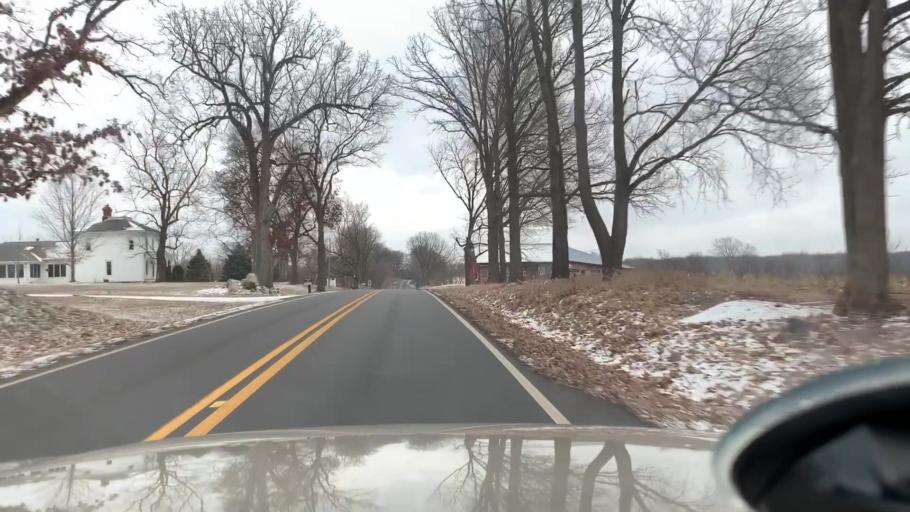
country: US
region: Michigan
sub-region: Jackson County
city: Spring Arbor
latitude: 42.2008
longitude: -84.5298
